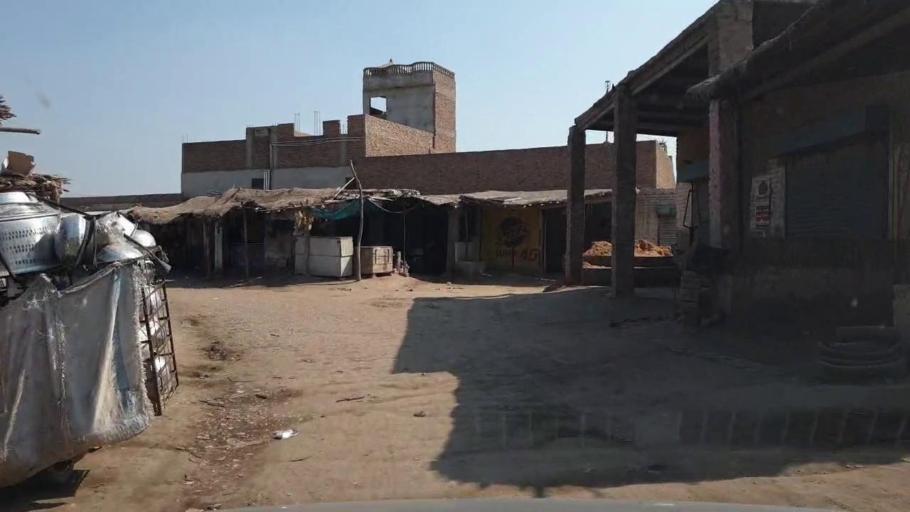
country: PK
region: Sindh
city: Tando Allahyar
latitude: 25.4240
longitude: 68.6523
